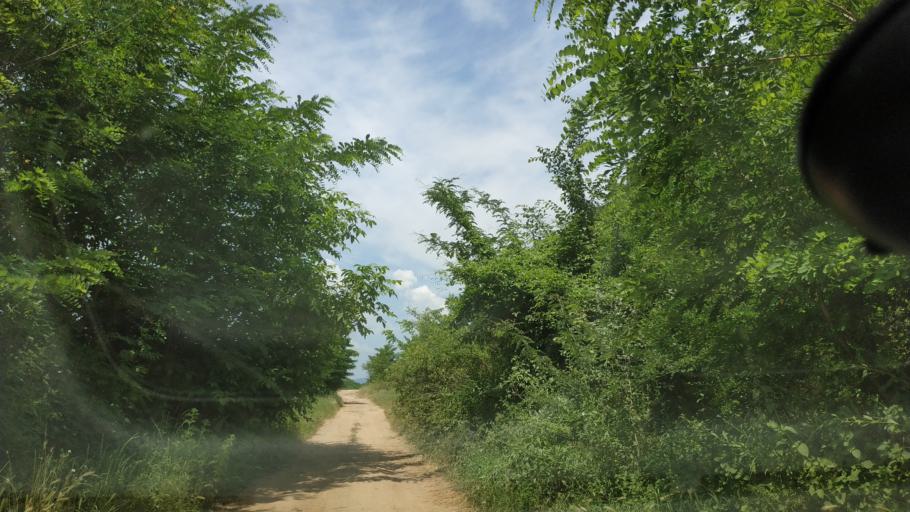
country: RS
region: Central Serbia
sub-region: Nisavski Okrug
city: Aleksinac
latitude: 43.5732
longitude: 21.7039
